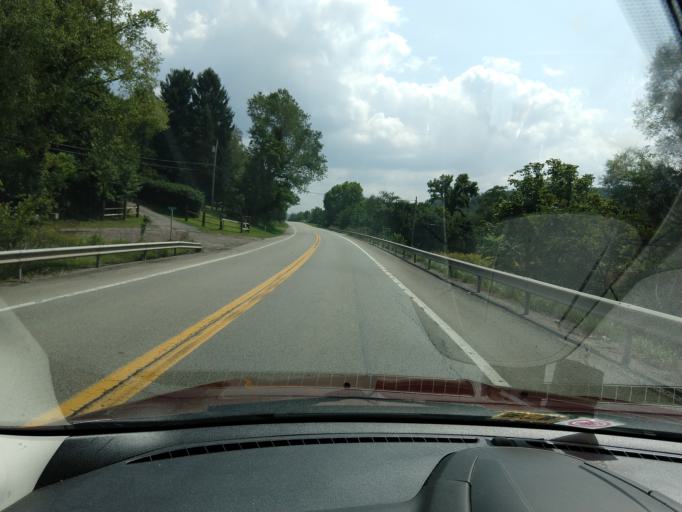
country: US
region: Pennsylvania
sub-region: Washington County
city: McGovern
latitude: 40.1723
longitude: -80.1356
